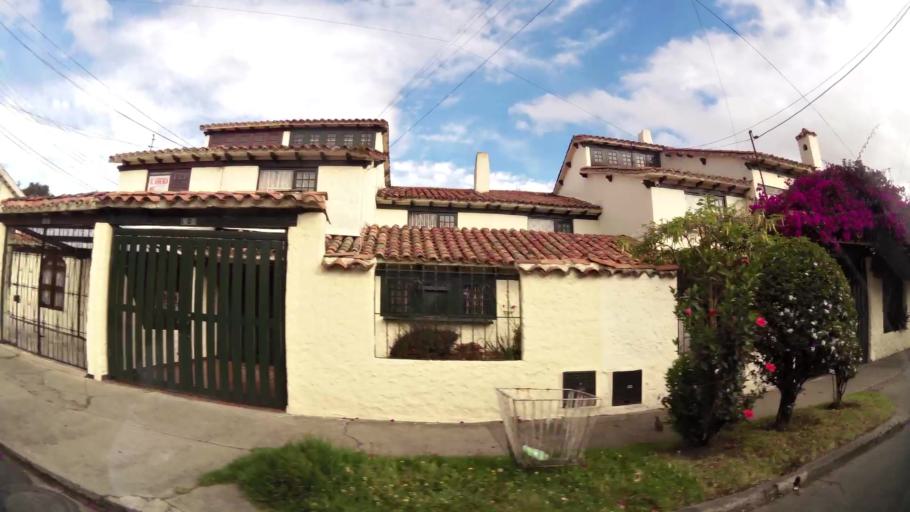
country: CO
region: Bogota D.C.
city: Barrio San Luis
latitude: 4.6927
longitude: -74.0726
